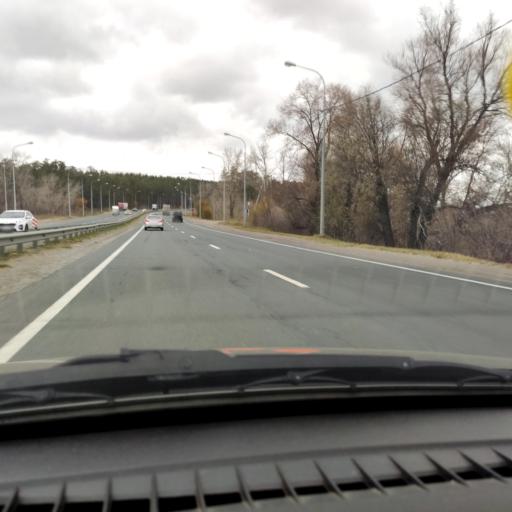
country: RU
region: Samara
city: Zhigulevsk
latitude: 53.5302
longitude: 49.5201
